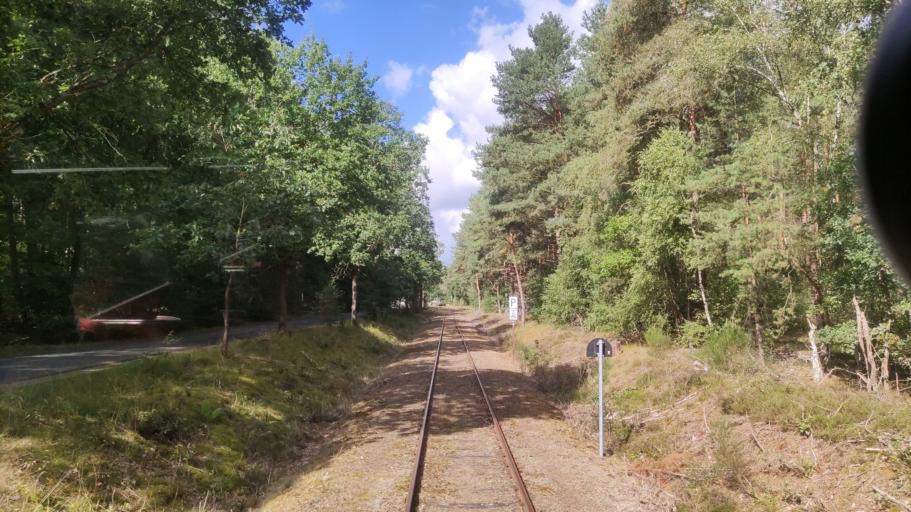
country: DE
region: Lower Saxony
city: Ludersburg
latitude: 53.2849
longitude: 10.5753
